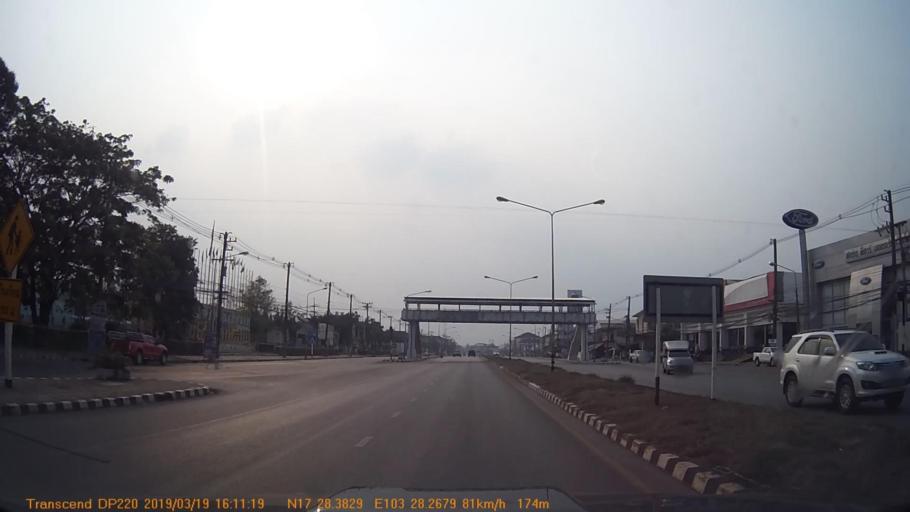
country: TH
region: Sakon Nakhon
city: Sawang Daen Din
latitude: 17.4732
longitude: 103.4705
